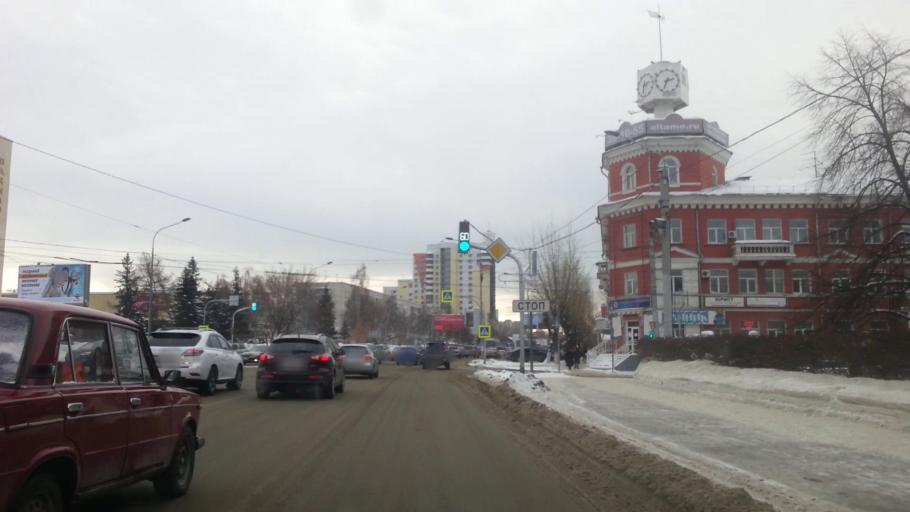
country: RU
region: Altai Krai
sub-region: Gorod Barnaulskiy
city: Barnaul
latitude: 53.3488
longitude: 83.7612
